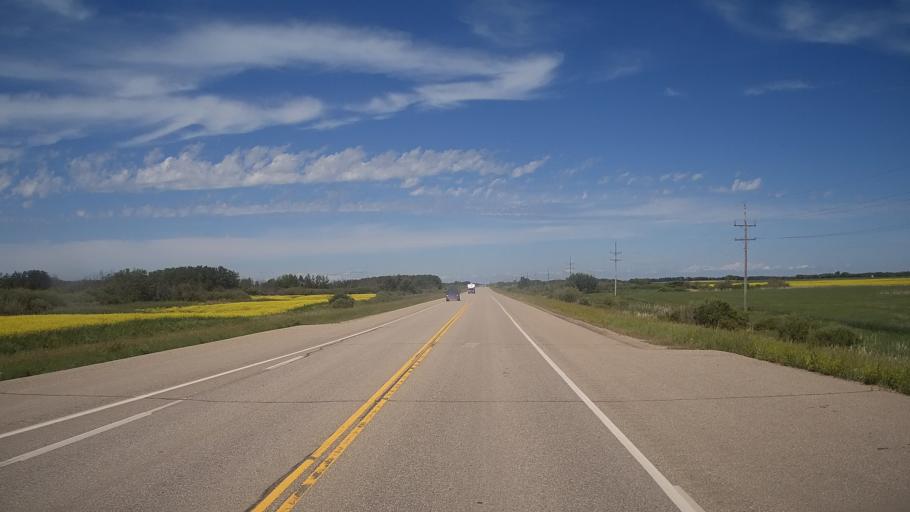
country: CA
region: Saskatchewan
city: Langenburg
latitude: 50.6400
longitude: -101.2760
